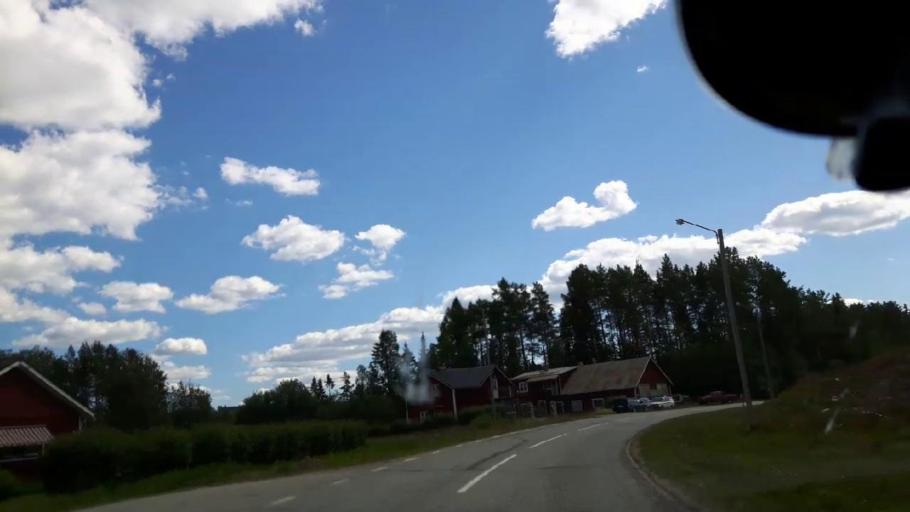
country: SE
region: Jaemtland
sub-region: Ragunda Kommun
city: Hammarstrand
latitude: 62.8893
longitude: 16.2257
